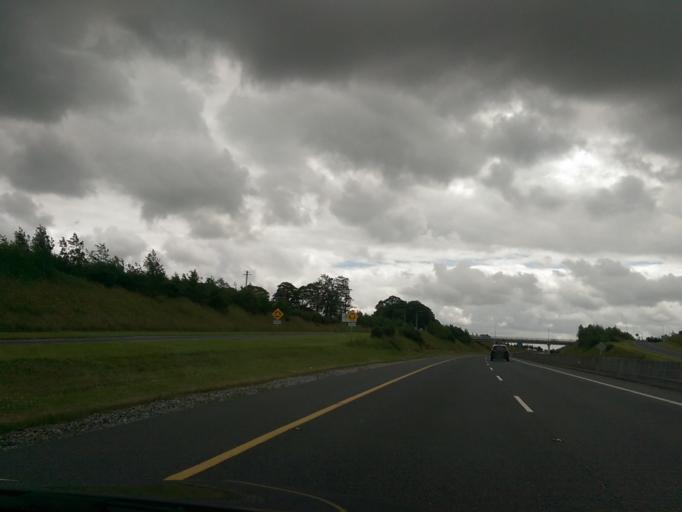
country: IE
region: Munster
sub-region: County Cork
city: Fermoy
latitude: 52.1656
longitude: -8.2669
